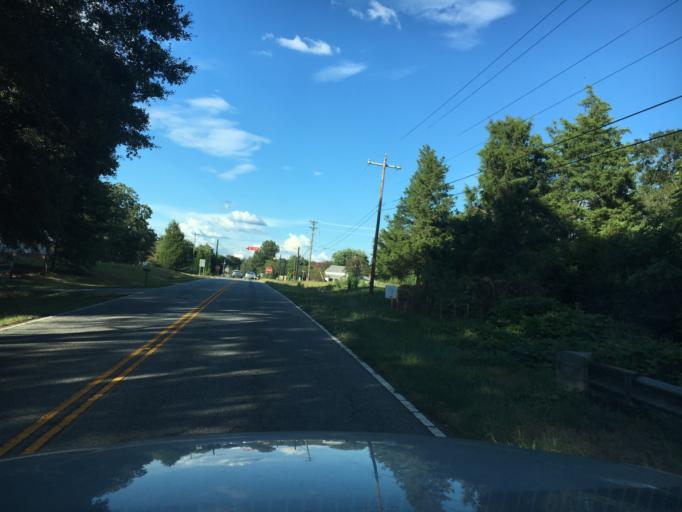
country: US
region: South Carolina
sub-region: Greenville County
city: Five Forks
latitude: 34.7608
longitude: -82.2033
